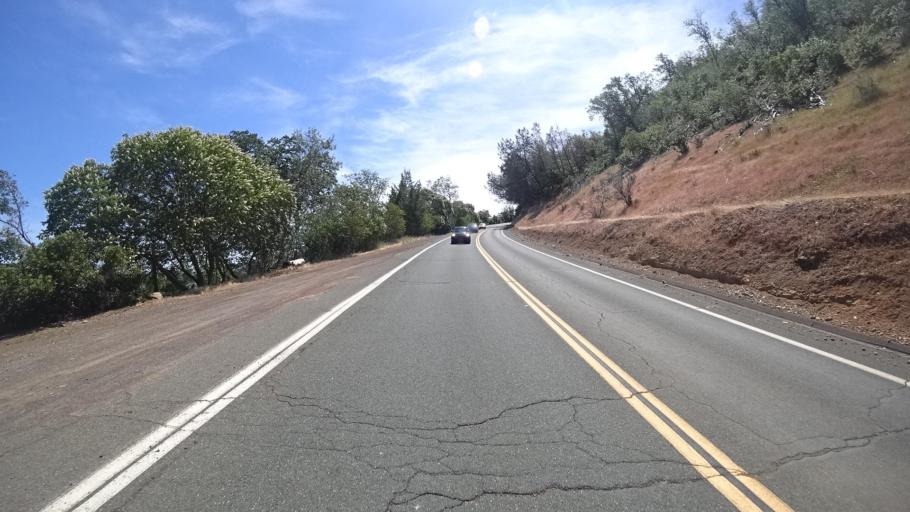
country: US
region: California
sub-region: Lake County
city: Clearlake
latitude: 38.9441
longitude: -122.6752
